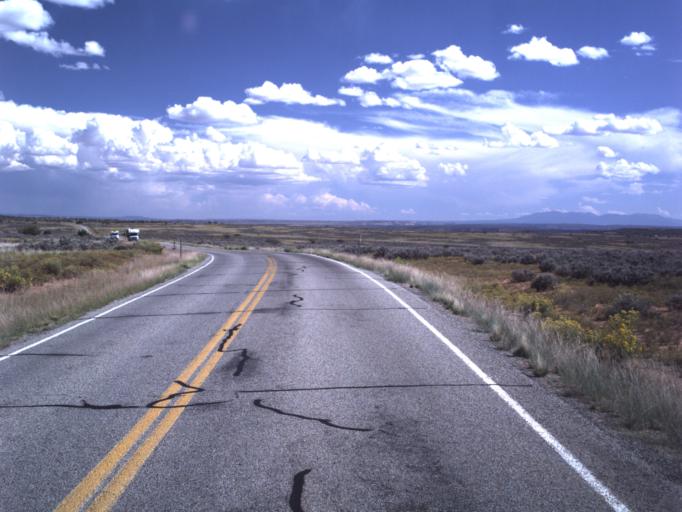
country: US
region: Utah
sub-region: Grand County
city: Moab
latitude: 38.5292
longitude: -109.7501
